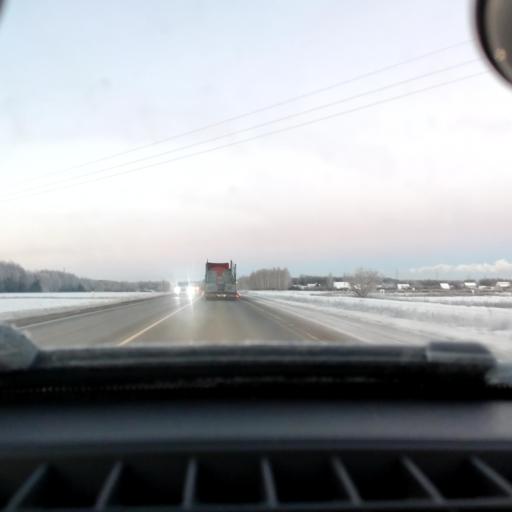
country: RU
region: Bashkortostan
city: Iglino
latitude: 54.7525
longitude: 56.3419
